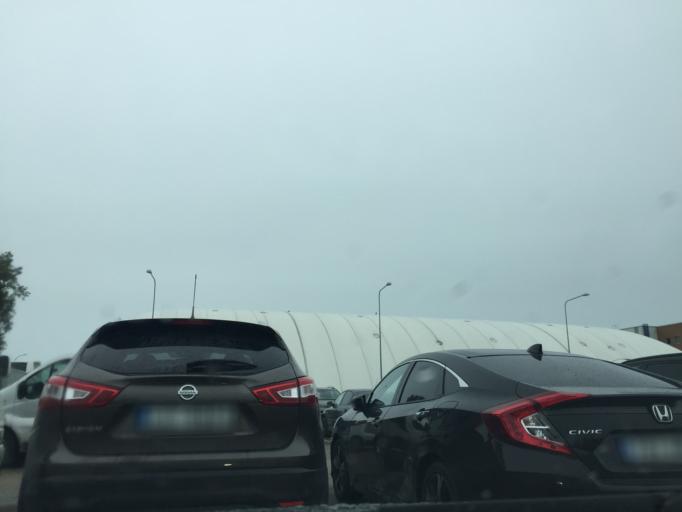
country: LV
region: Babite
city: Pinki
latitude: 56.9754
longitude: 23.8608
